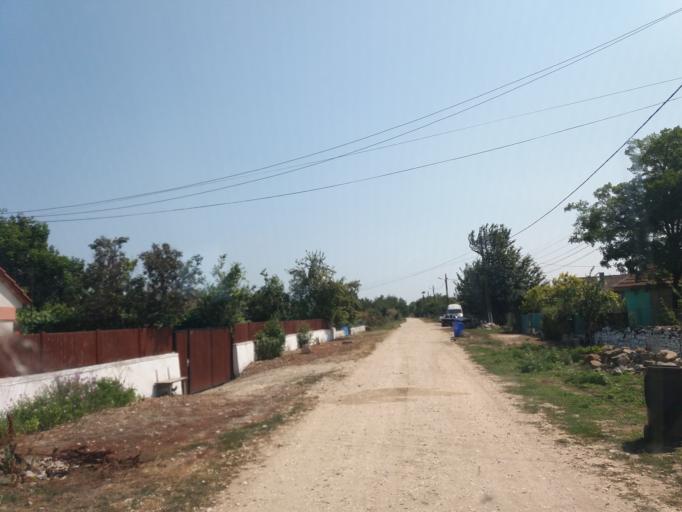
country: RO
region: Constanta
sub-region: Comuna Sacele
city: Sacele
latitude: 44.4567
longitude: 28.7383
